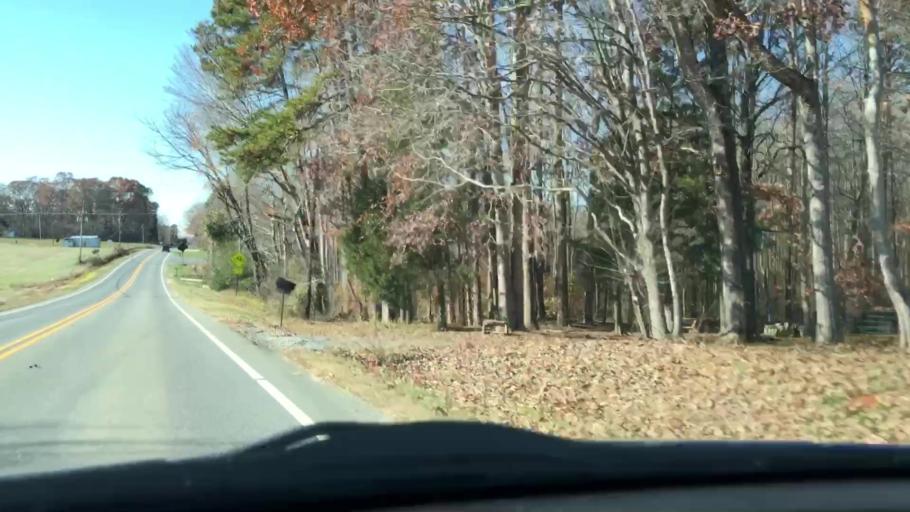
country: US
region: North Carolina
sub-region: Randolph County
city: Asheboro
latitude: 35.6737
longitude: -79.9148
